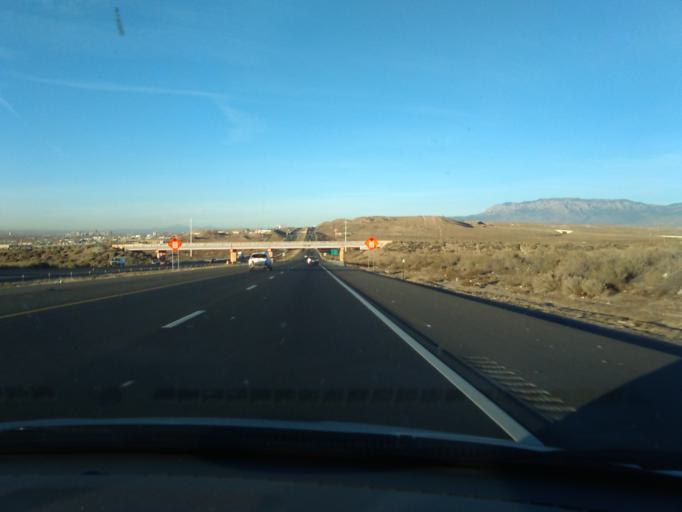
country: US
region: New Mexico
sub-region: Bernalillo County
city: South Valley
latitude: 34.9968
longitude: -106.6464
